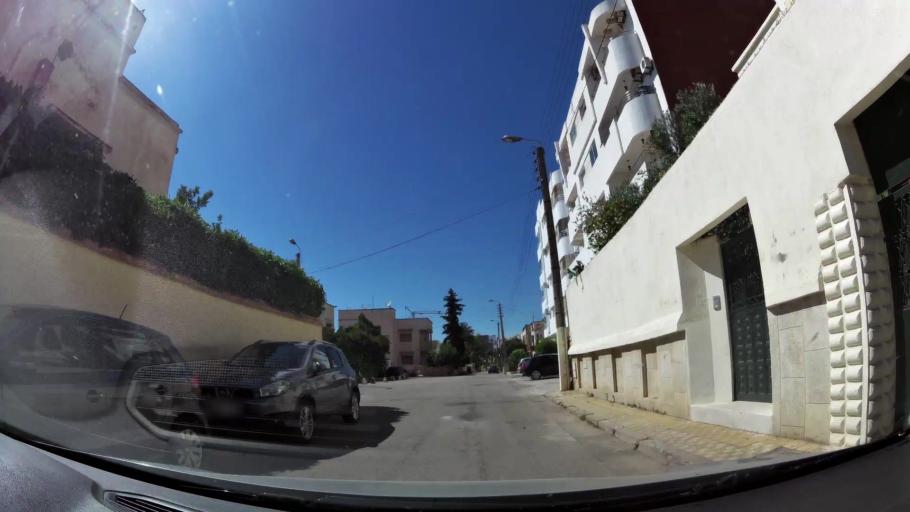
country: MA
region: Fes-Boulemane
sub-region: Fes
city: Fes
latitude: 34.0236
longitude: -4.9905
